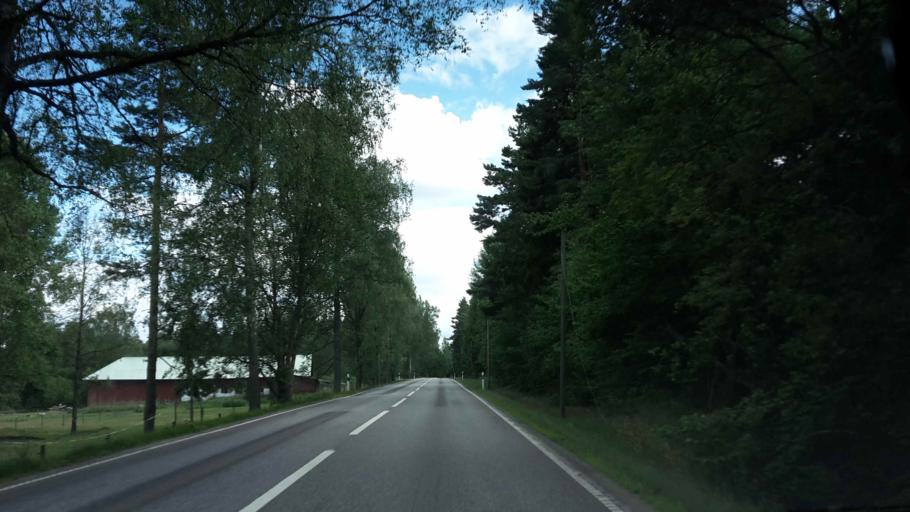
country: SE
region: OErebro
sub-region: Hallsbergs Kommun
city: Palsboda
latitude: 58.8175
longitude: 15.4133
